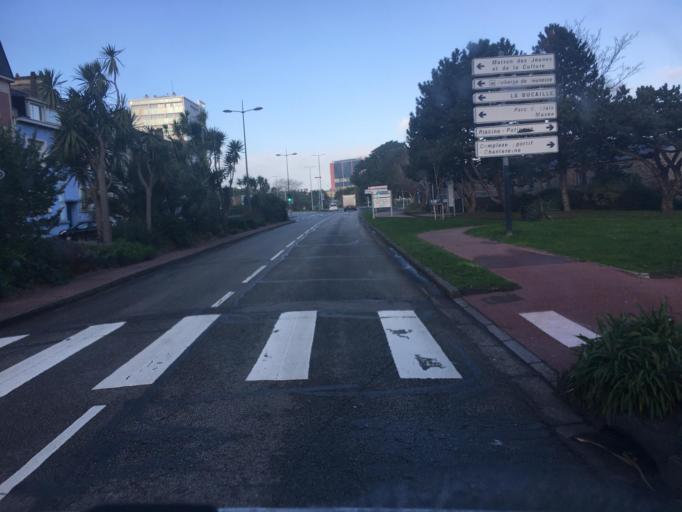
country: FR
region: Lower Normandy
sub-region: Departement de la Manche
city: Cherbourg-Octeville
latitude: 49.6439
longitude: -1.6260
